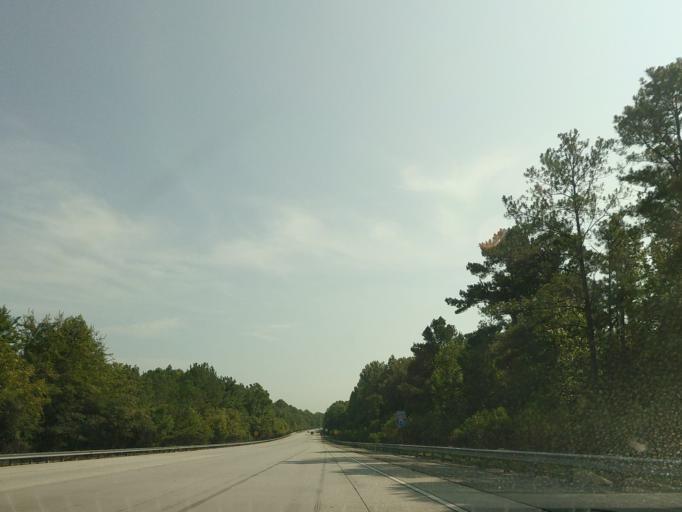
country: US
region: Georgia
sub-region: Bibb County
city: West Point
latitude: 32.7605
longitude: -83.7055
